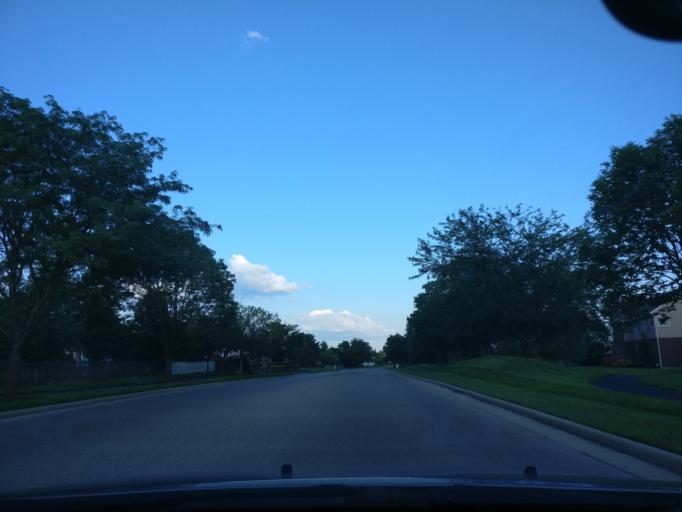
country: US
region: Ohio
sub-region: Warren County
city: Five Points
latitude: 39.5789
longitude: -84.2202
